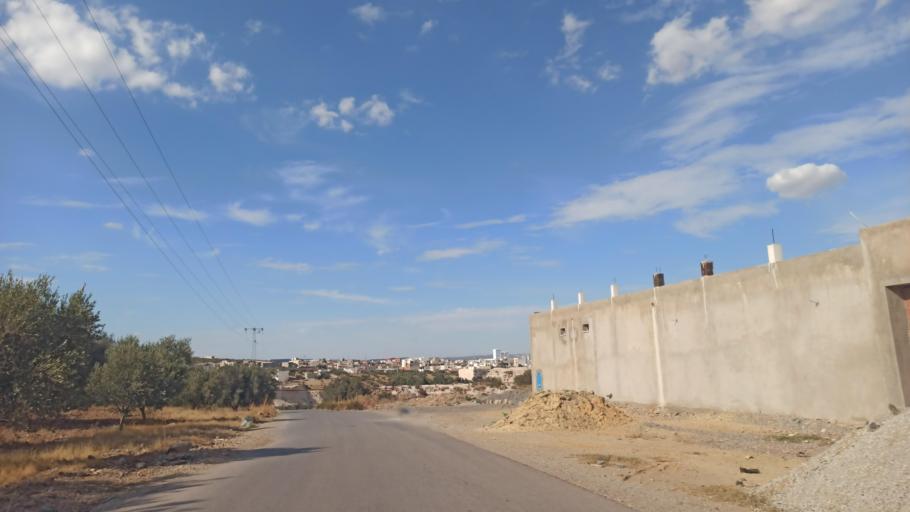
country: TN
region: Zaghwan
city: Zaghouan
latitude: 36.3404
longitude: 10.2092
